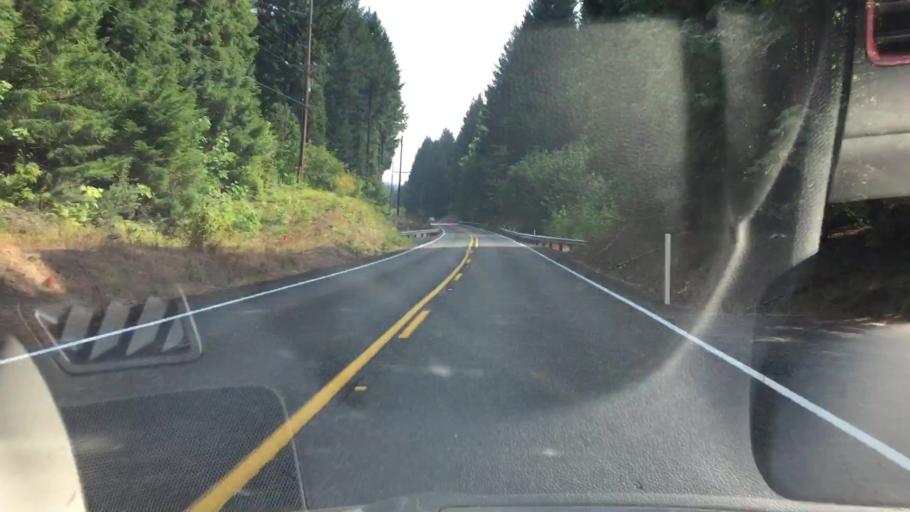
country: US
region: Washington
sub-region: Klickitat County
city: White Salmon
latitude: 45.8775
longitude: -121.5199
